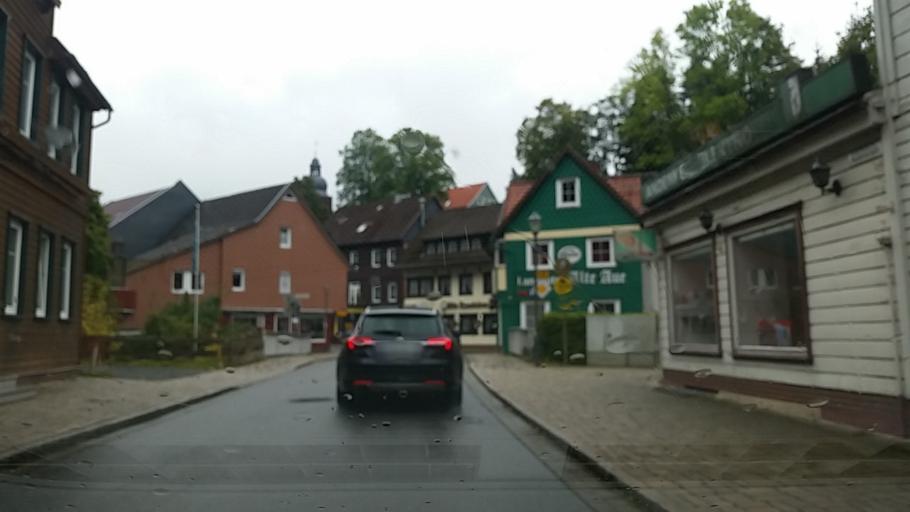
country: DE
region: Lower Saxony
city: Altenau
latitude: 51.8039
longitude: 10.4443
